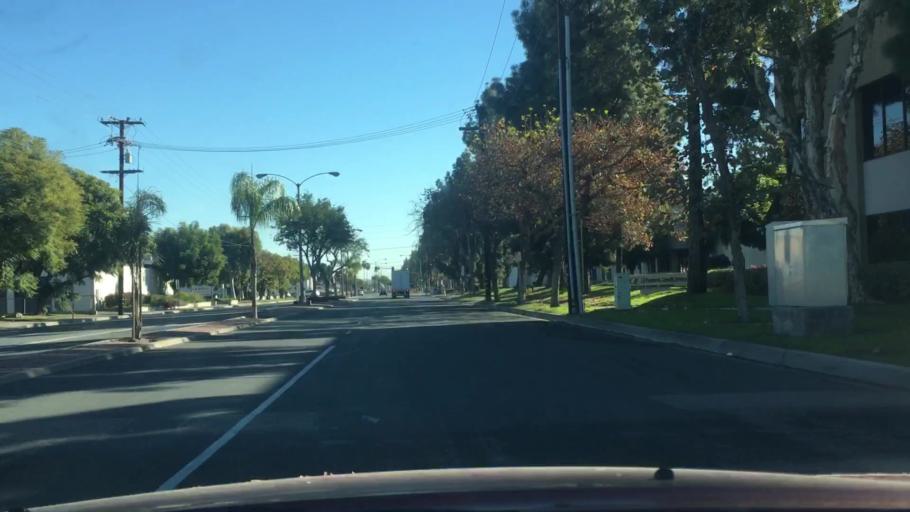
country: US
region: California
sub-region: Los Angeles County
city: Cerritos
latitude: 33.8878
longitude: -118.0490
